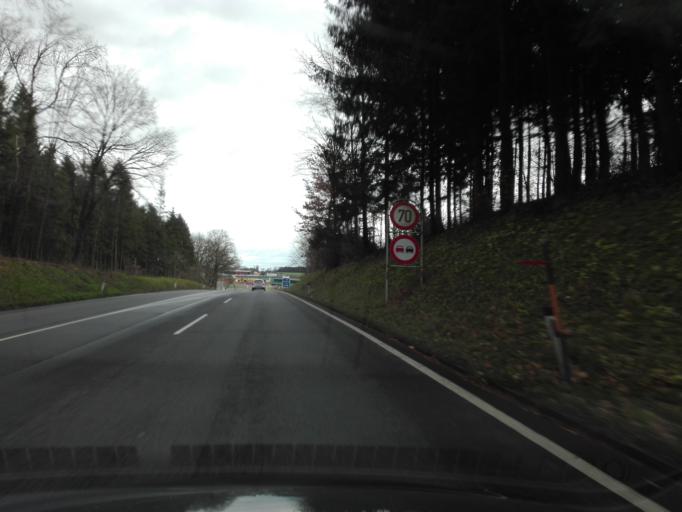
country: AT
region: Lower Austria
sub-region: Politischer Bezirk Amstetten
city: Zeillern
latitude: 48.1171
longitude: 14.7249
